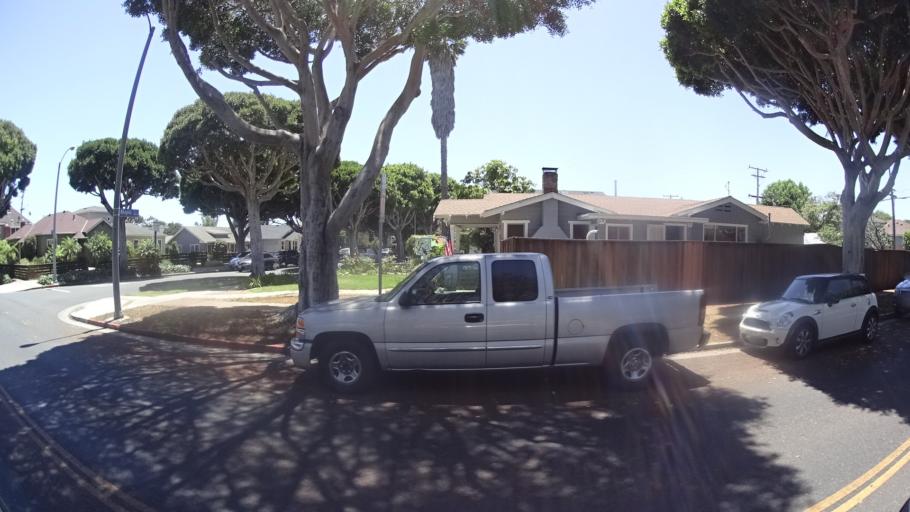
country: US
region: California
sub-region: Los Angeles County
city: Santa Monica
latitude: 34.0092
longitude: -118.4746
